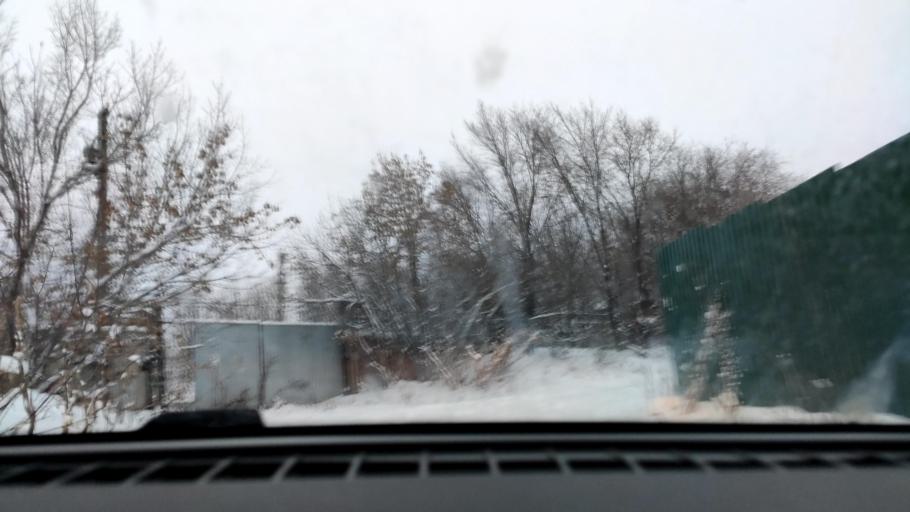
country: RU
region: Samara
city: Samara
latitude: 53.1809
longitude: 50.1864
